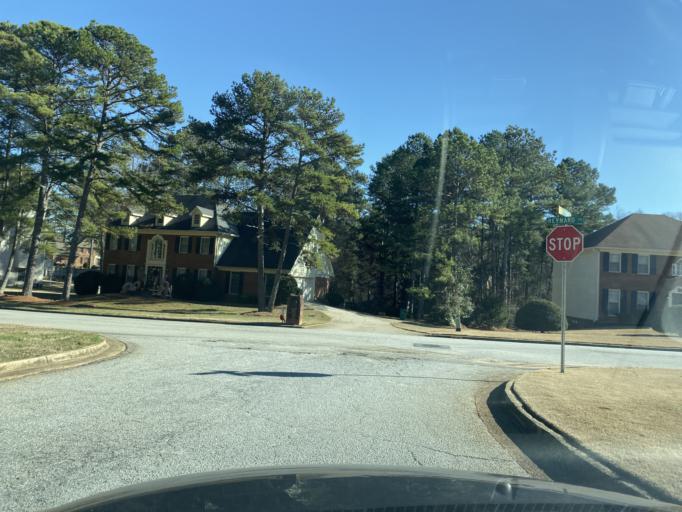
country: US
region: Georgia
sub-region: DeKalb County
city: Pine Mountain
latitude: 33.6820
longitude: -84.1619
